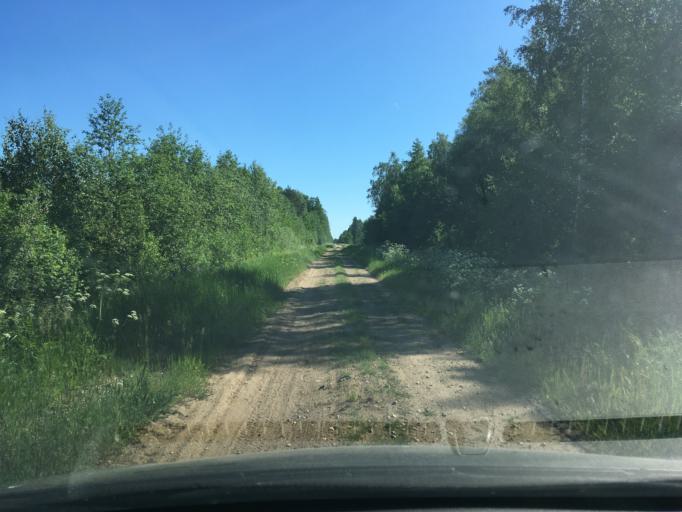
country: EE
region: Laeaene
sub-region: Lihula vald
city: Lihula
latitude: 58.6353
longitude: 23.7525
